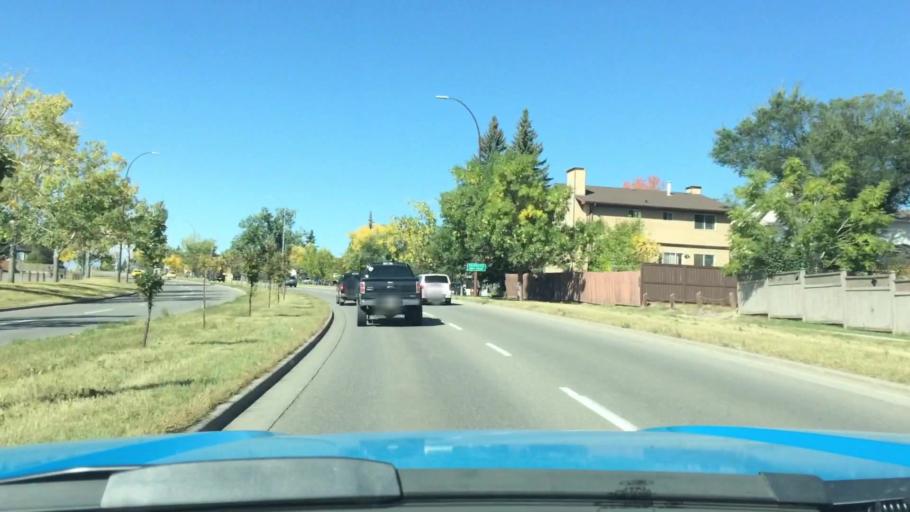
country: CA
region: Alberta
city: Calgary
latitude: 50.9138
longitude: -114.0791
